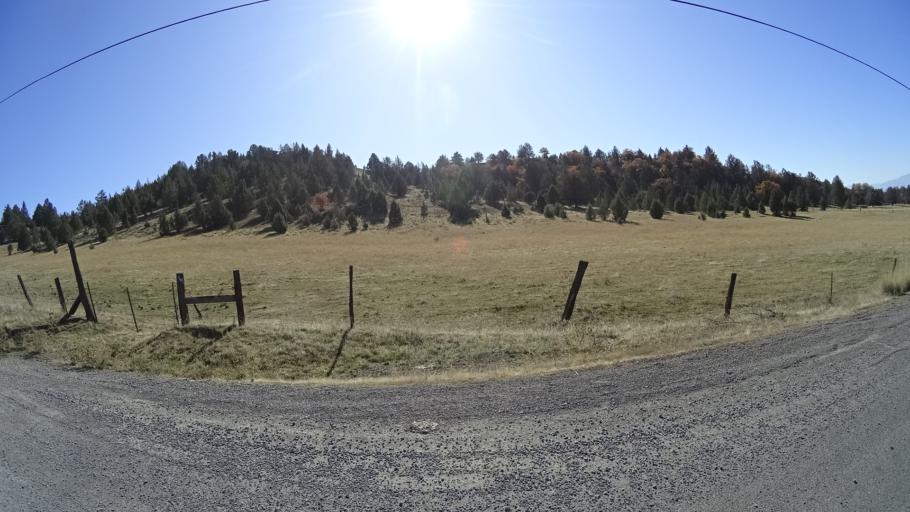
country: US
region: California
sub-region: Siskiyou County
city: Montague
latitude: 41.8084
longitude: -122.3768
